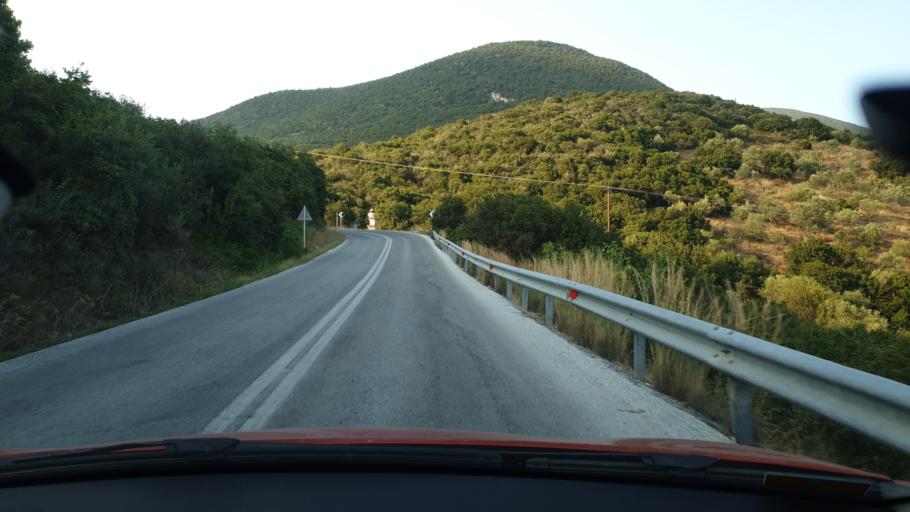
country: GR
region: Thessaly
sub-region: Nomos Magnisias
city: Pteleos
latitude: 39.0567
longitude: 22.9367
